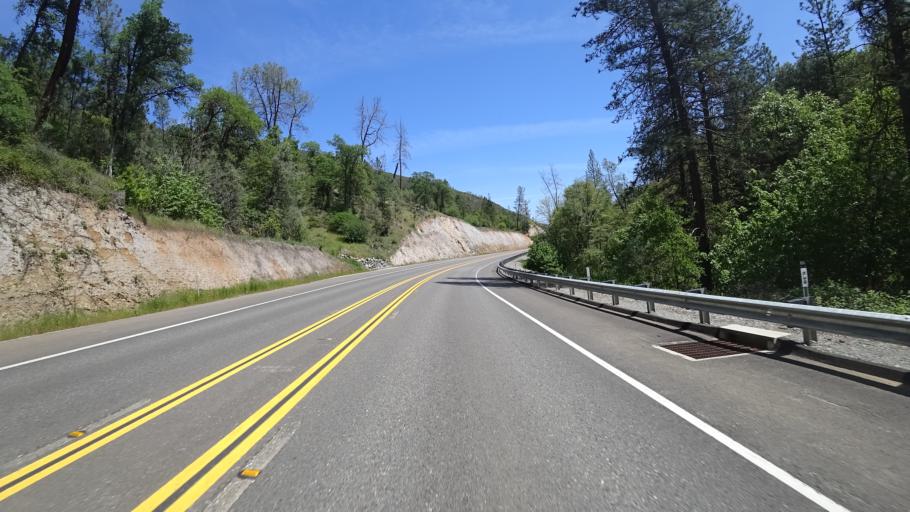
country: US
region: California
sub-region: Trinity County
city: Lewiston
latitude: 40.6741
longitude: -122.6679
